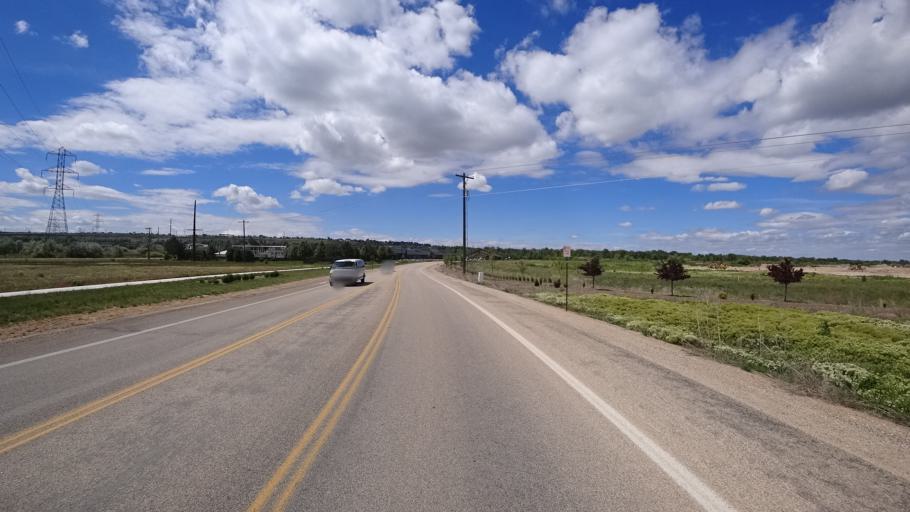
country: US
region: Idaho
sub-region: Ada County
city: Boise
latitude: 43.5707
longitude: -116.1264
